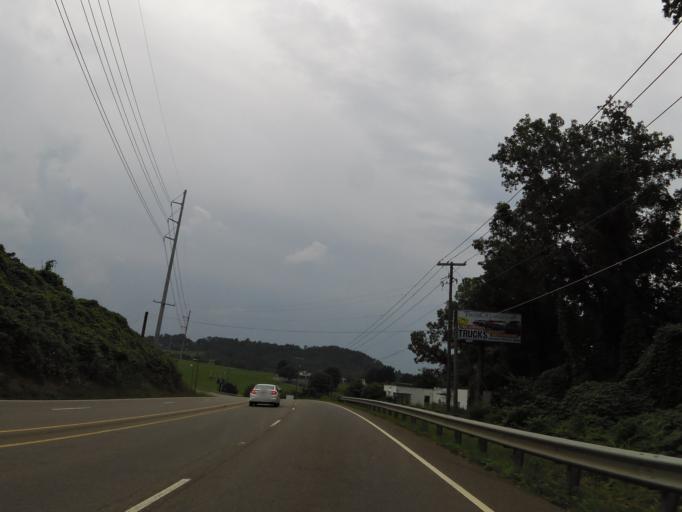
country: US
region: Tennessee
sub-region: Sevier County
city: Seymour
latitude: 35.8907
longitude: -83.7962
